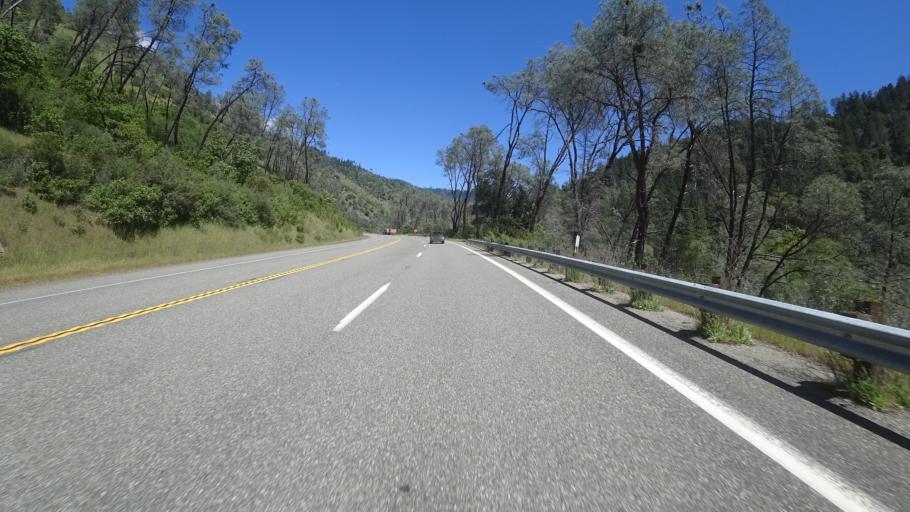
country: US
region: California
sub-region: Trinity County
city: Hayfork
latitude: 40.7355
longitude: -123.2291
